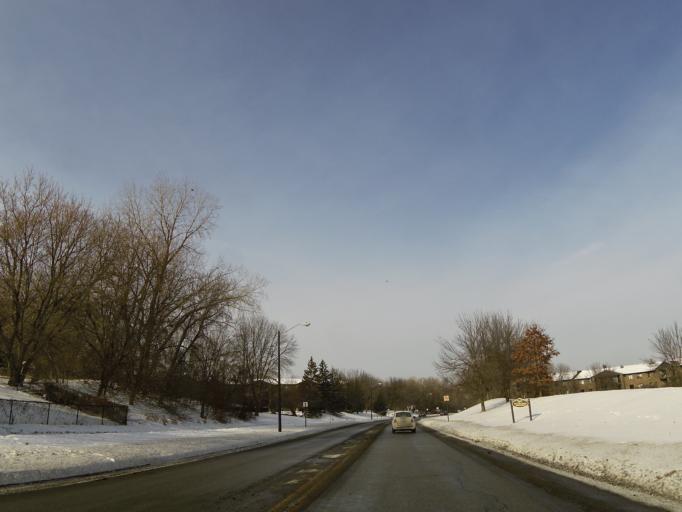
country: US
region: Minnesota
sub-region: Hennepin County
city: Eden Prairie
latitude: 44.8498
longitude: -93.4516
